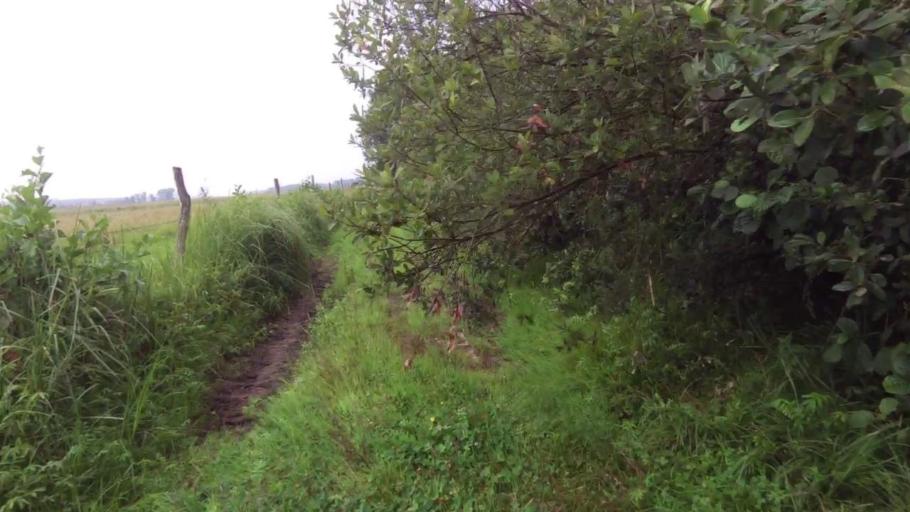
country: PL
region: West Pomeranian Voivodeship
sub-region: Powiat stargardzki
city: Suchan
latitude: 53.2507
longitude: 15.4008
